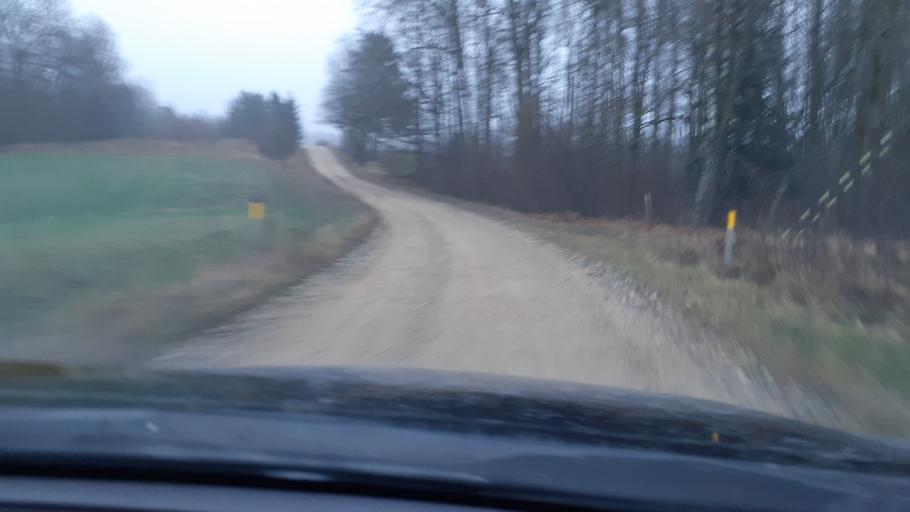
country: LV
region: Alsunga
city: Alsunga
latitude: 56.8765
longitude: 21.7184
